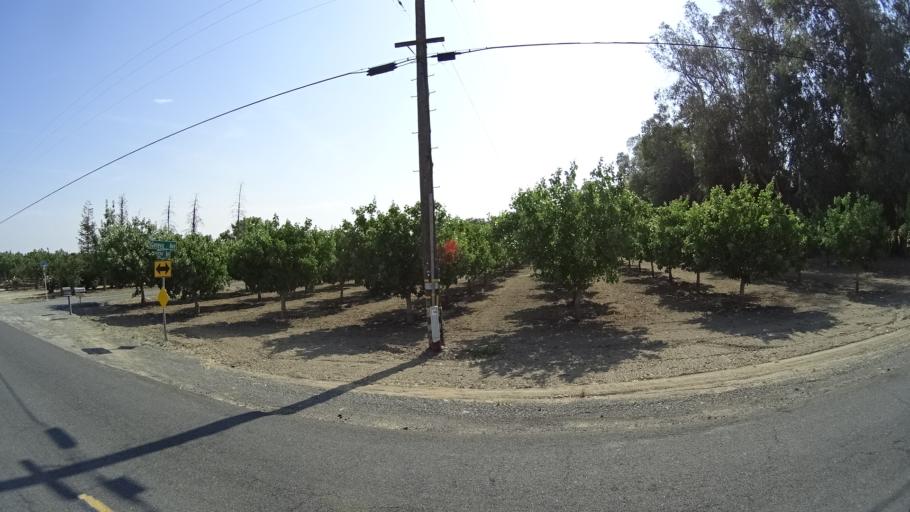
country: US
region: California
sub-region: Kings County
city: Lemoore
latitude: 36.3366
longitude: -119.8512
